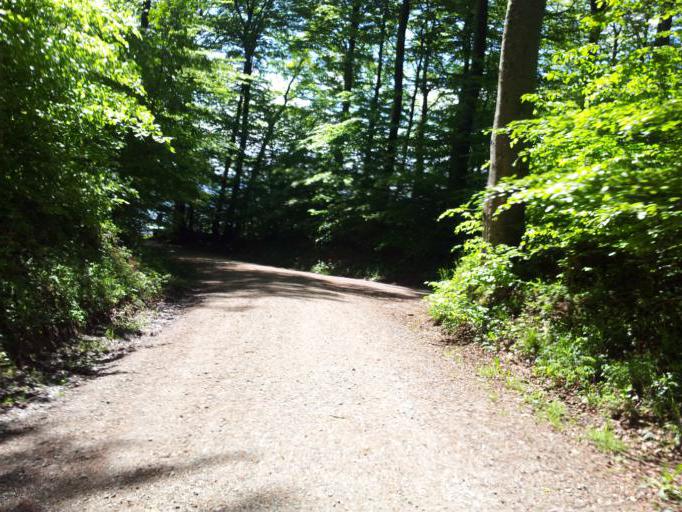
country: CH
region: Aargau
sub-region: Bezirk Baden
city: Spreitenbach
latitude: 47.3994
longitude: 8.3522
